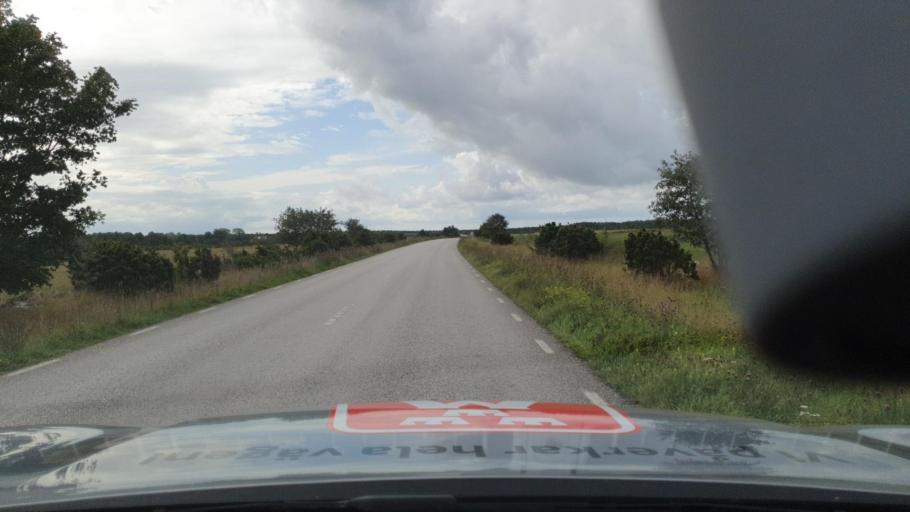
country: SE
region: Gotland
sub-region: Gotland
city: Hemse
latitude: 57.1388
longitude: 18.2838
